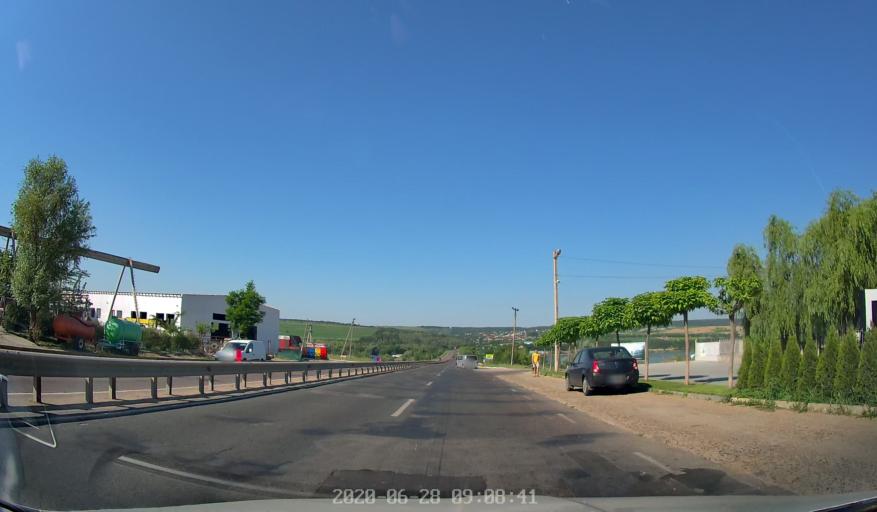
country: MD
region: Laloveni
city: Ialoveni
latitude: 46.9593
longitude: 28.7502
